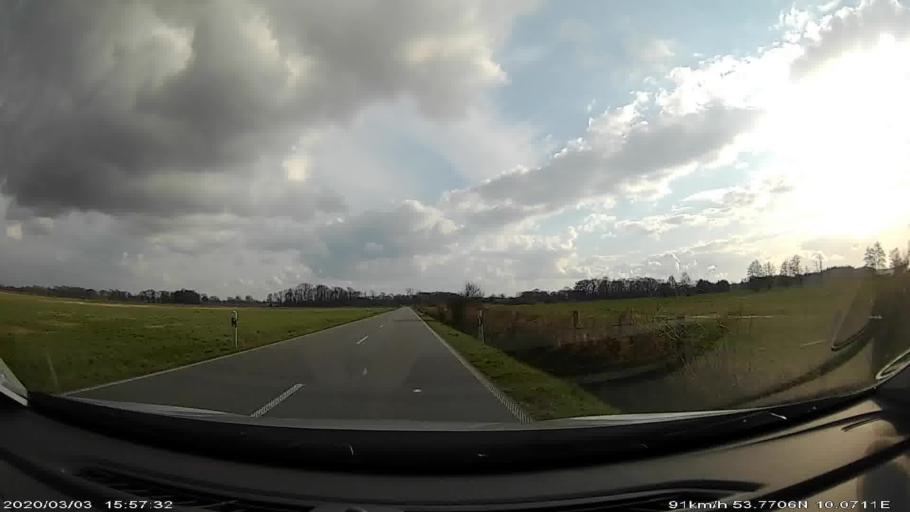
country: DE
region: Schleswig-Holstein
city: Tangstedt
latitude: 53.7720
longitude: 10.0712
